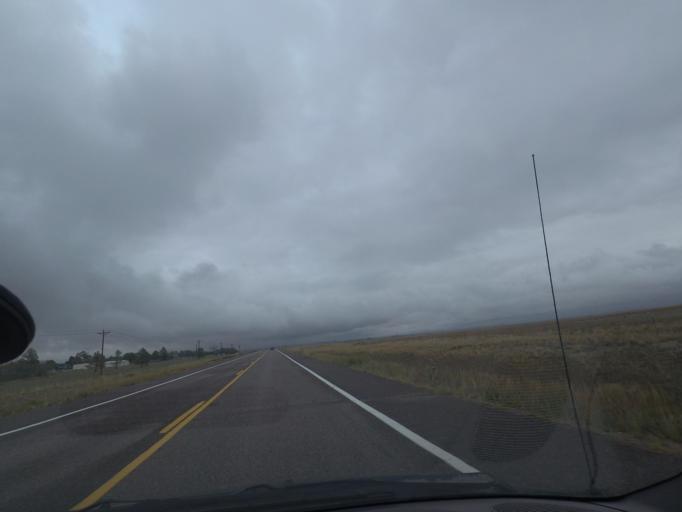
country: US
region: Colorado
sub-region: Arapahoe County
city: Byers
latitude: 39.7400
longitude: -104.0492
